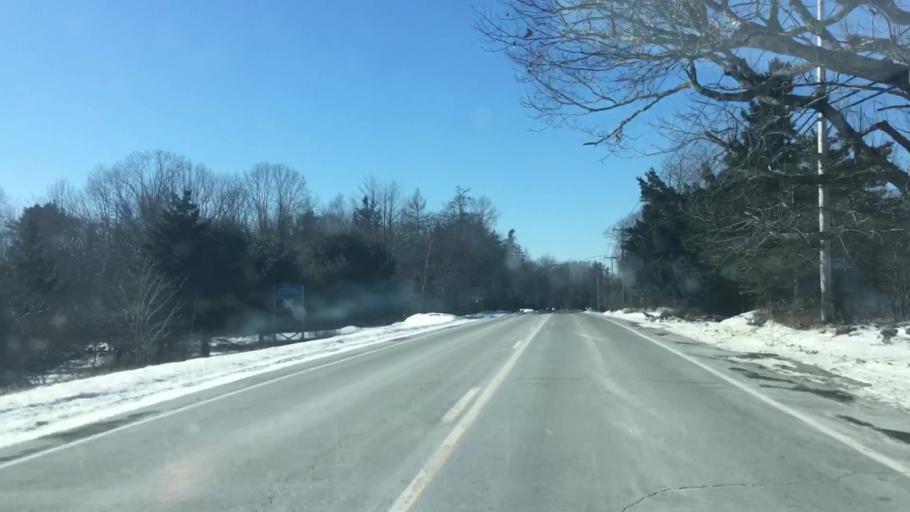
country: US
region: Maine
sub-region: Hancock County
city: Surry
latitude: 44.4933
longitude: -68.4556
